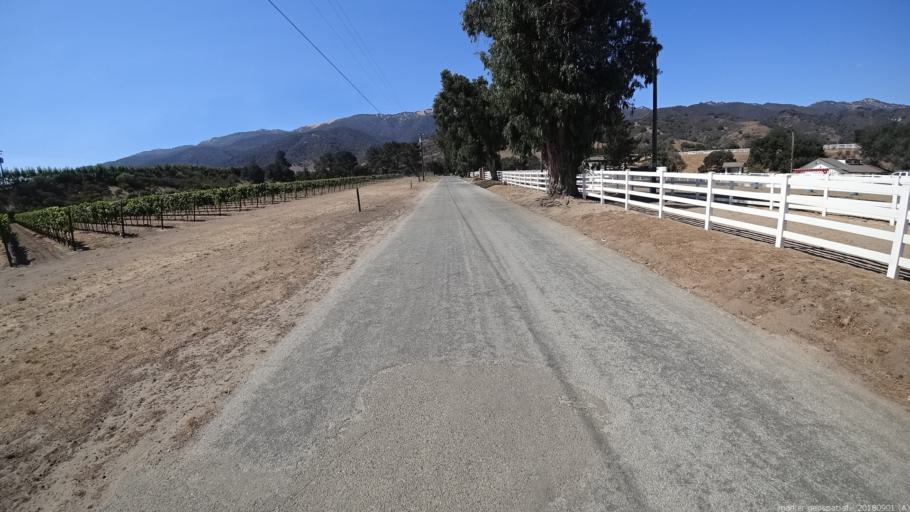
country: US
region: California
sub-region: Monterey County
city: Chualar
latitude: 36.5180
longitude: -121.5250
